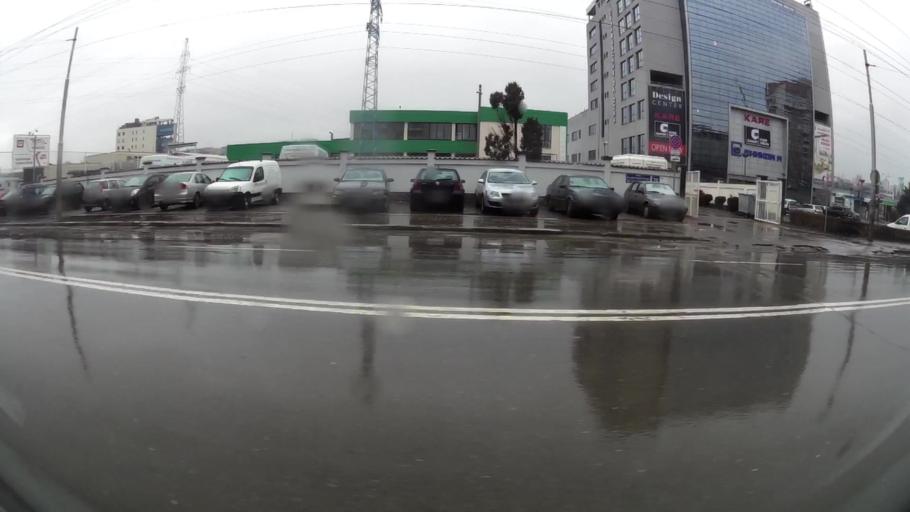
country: BG
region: Sofia-Capital
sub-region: Stolichna Obshtina
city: Sofia
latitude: 42.6613
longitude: 23.3935
